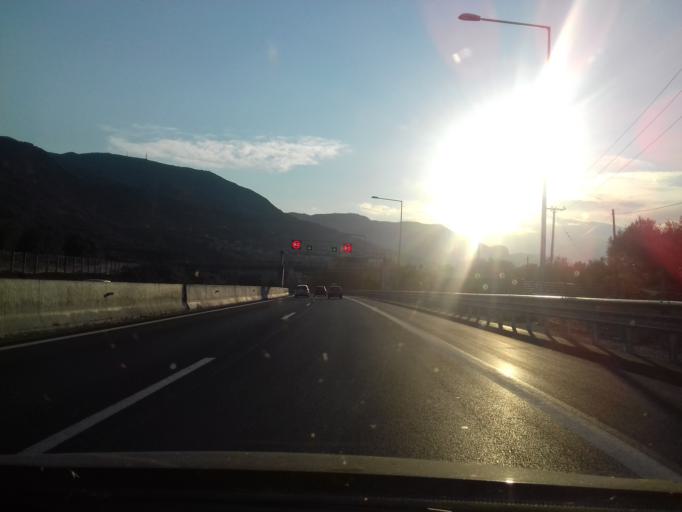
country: GR
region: West Greece
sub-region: Nomos Achaias
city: Akrata
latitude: 38.1714
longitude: 22.2898
